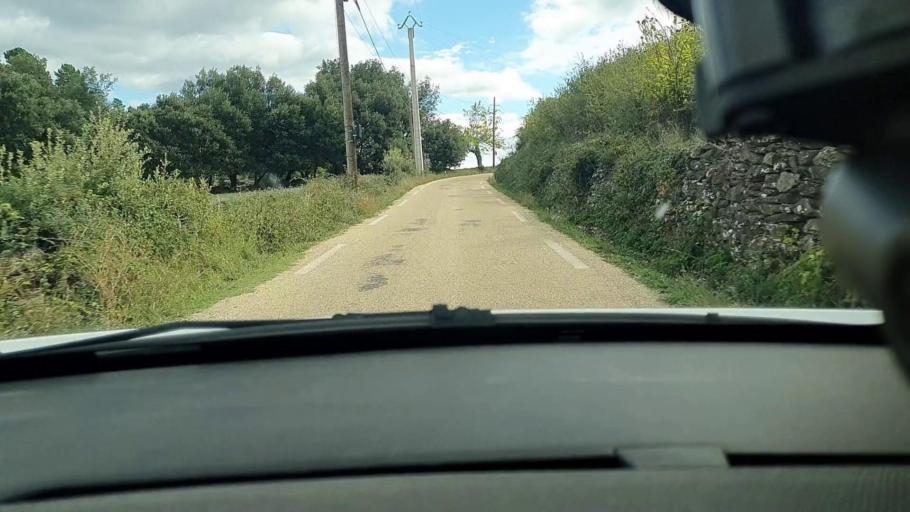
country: FR
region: Languedoc-Roussillon
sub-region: Departement du Gard
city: Besseges
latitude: 44.3091
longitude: 4.0241
